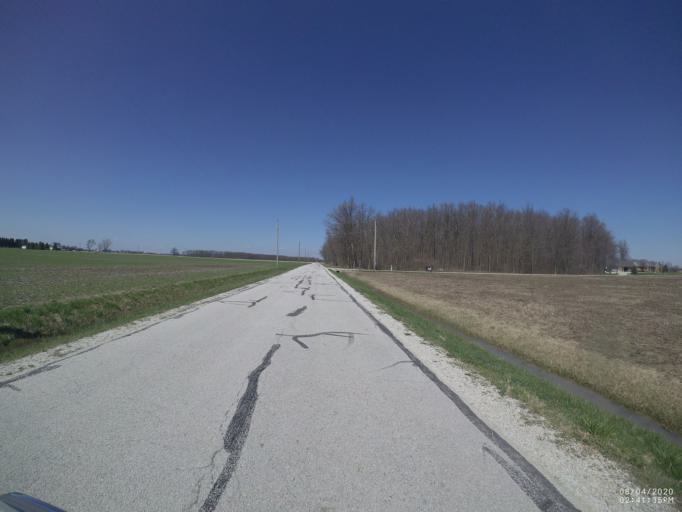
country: US
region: Ohio
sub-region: Sandusky County
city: Gibsonburg
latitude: 41.2878
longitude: -83.2968
